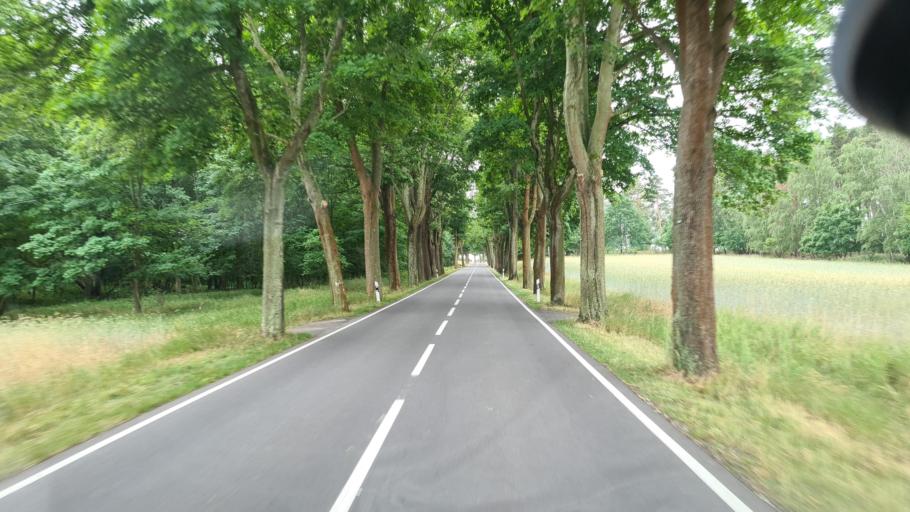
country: DE
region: Brandenburg
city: Ihlow
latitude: 51.9692
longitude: 13.2509
